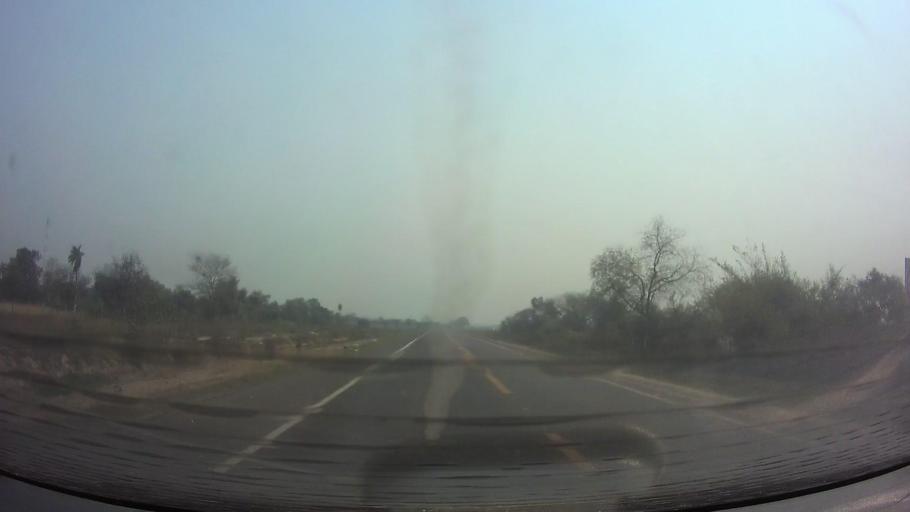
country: PY
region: Central
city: Limpio
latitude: -25.1523
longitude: -57.4784
